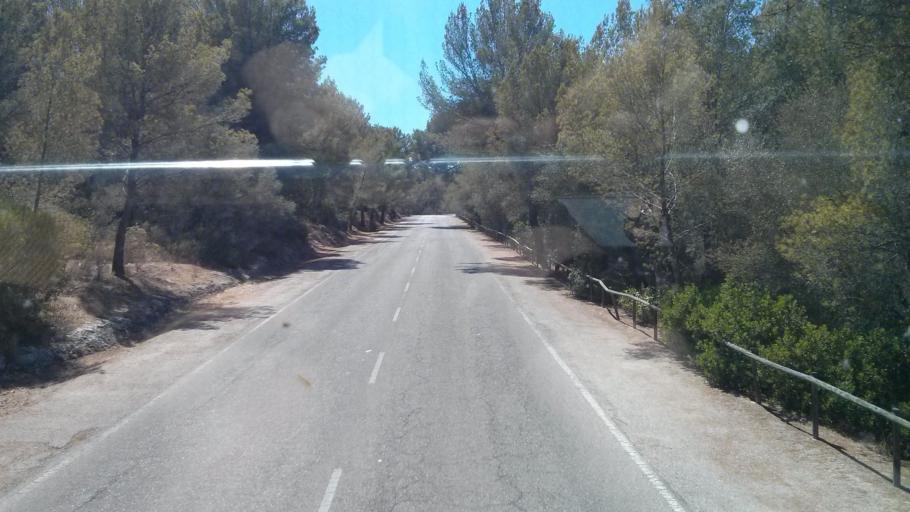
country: ES
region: Balearic Islands
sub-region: Illes Balears
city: Palma
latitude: 39.5688
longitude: 2.6206
